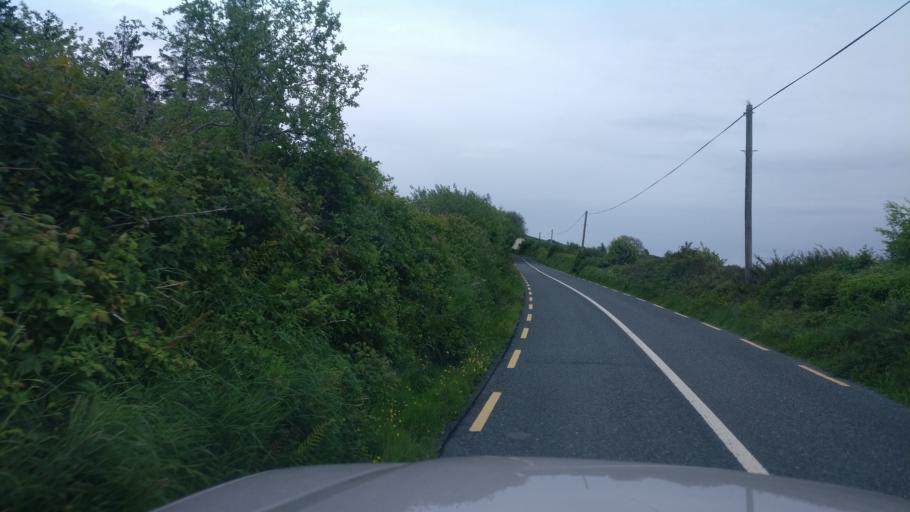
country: IE
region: Connaught
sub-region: County Galway
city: Loughrea
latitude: 53.0561
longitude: -8.6451
